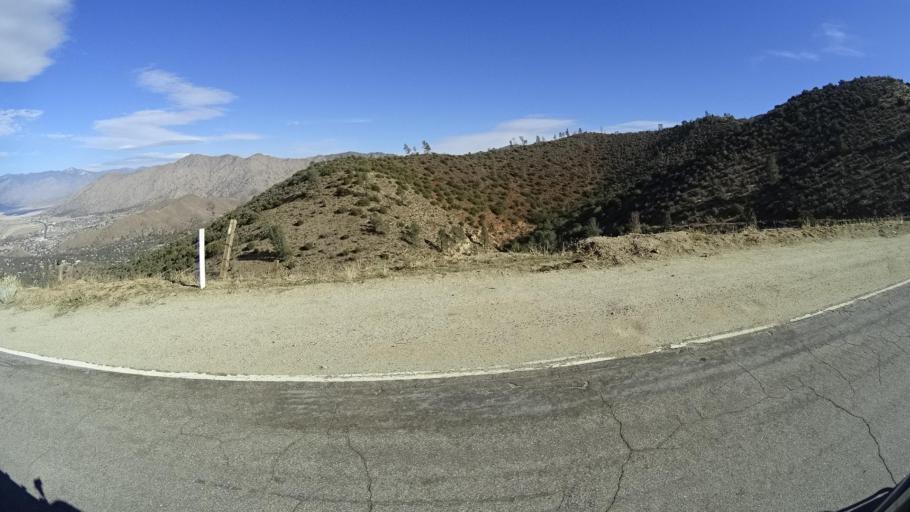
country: US
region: California
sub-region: Kern County
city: Bodfish
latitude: 35.5732
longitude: -118.5069
